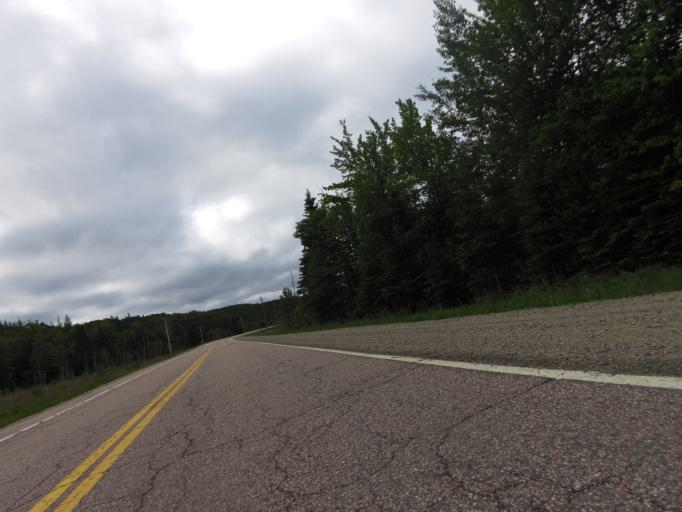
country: CA
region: Quebec
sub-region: Outaouais
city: Shawville
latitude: 45.8149
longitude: -76.4601
